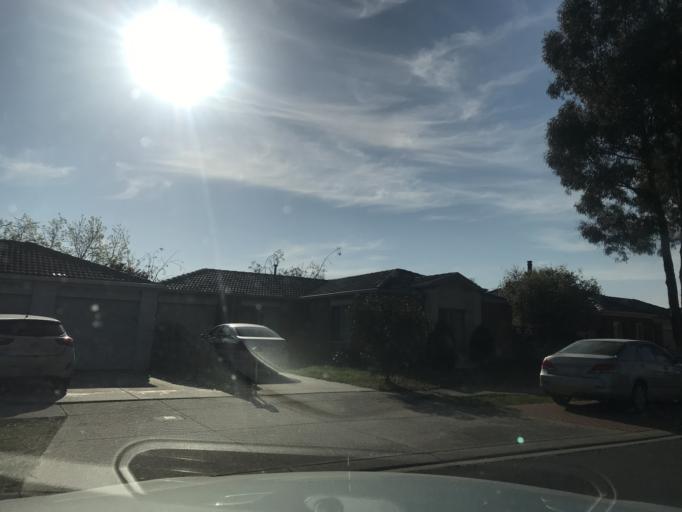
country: AU
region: Victoria
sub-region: Wyndham
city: Williams Landing
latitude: -37.8566
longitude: 144.7187
